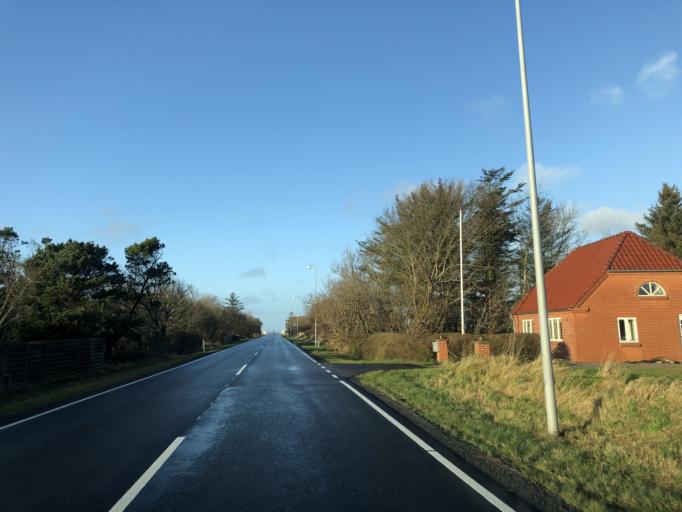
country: DK
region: Central Jutland
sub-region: Struer Kommune
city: Struer
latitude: 56.5543
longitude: 8.4784
